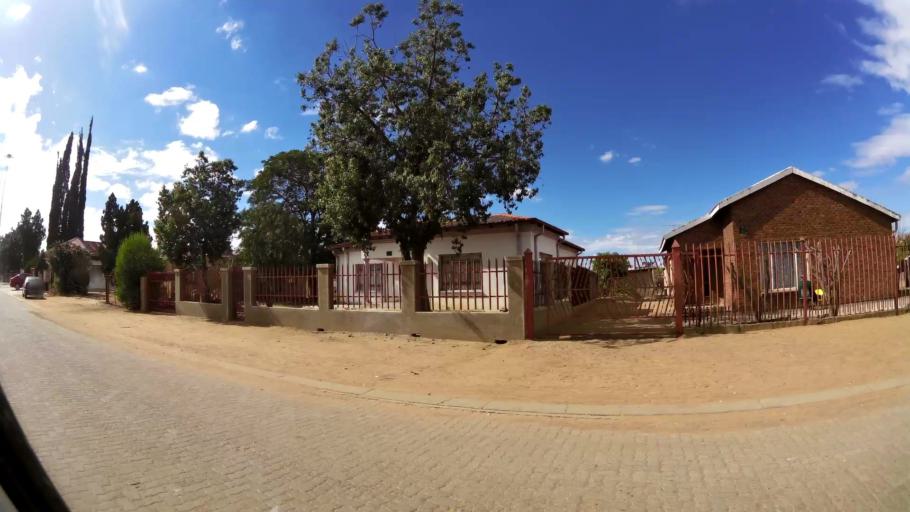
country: ZA
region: Limpopo
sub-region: Waterberg District Municipality
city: Bela-Bela
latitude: -24.8879
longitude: 28.3064
